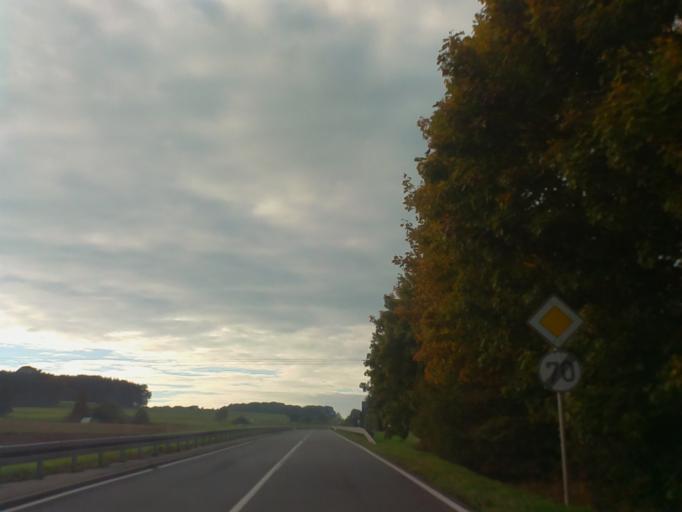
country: DE
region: Hesse
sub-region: Regierungsbezirk Darmstadt
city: Brensbach
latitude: 49.7758
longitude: 8.9390
